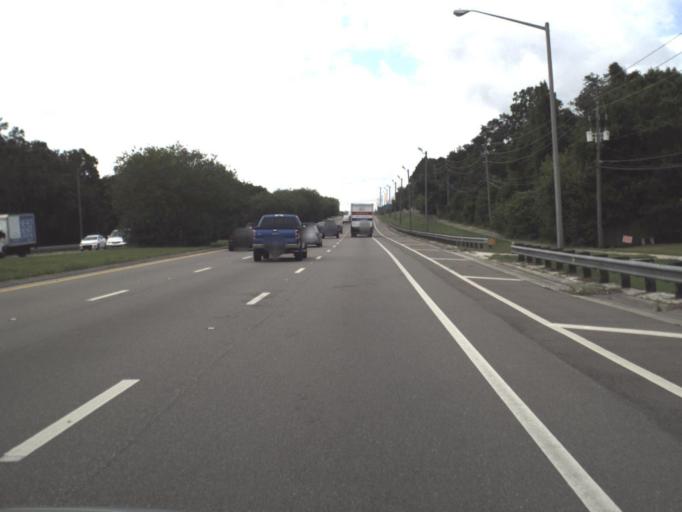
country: US
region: Florida
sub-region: Pinellas County
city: Saint George
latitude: 28.0470
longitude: -82.7093
